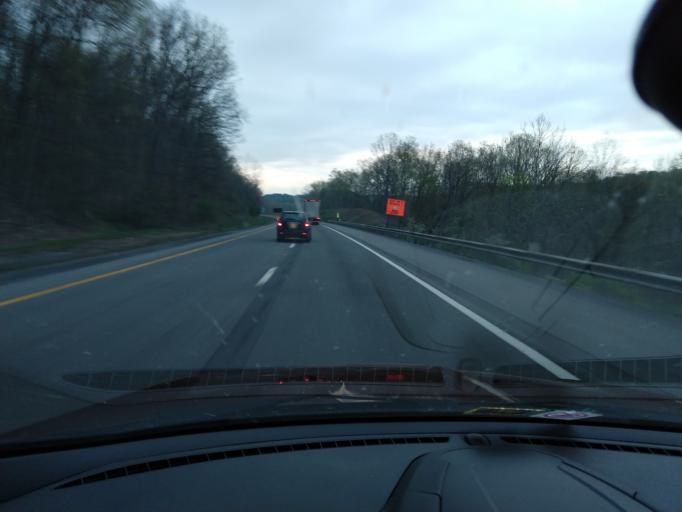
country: US
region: West Virginia
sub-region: Braxton County
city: Sutton
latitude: 38.6889
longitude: -80.6845
